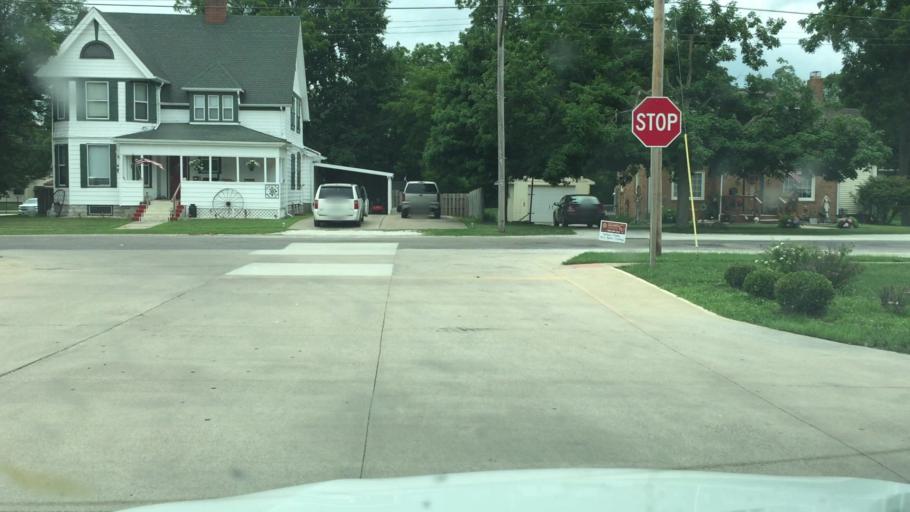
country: US
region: Illinois
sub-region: Hancock County
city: Carthage
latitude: 40.4164
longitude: -91.1271
